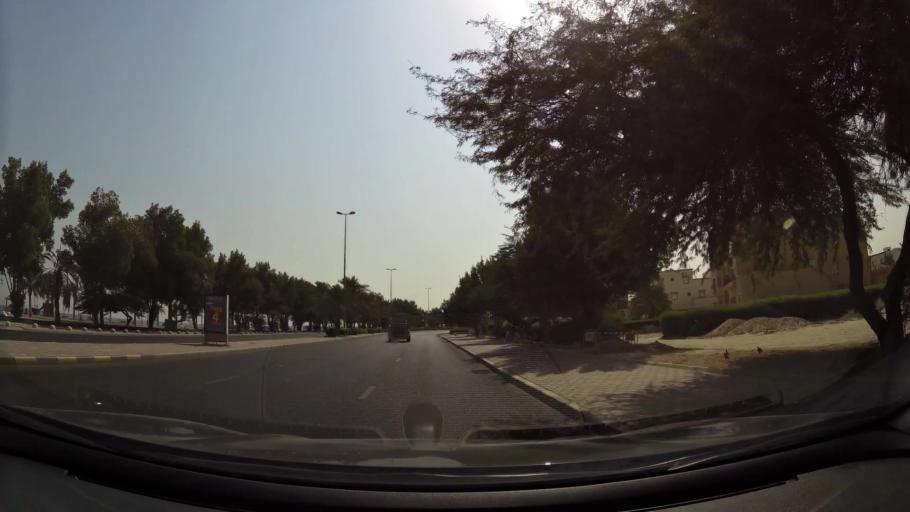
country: KW
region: Al Ahmadi
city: Al Fintas
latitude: 29.1781
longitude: 48.1214
